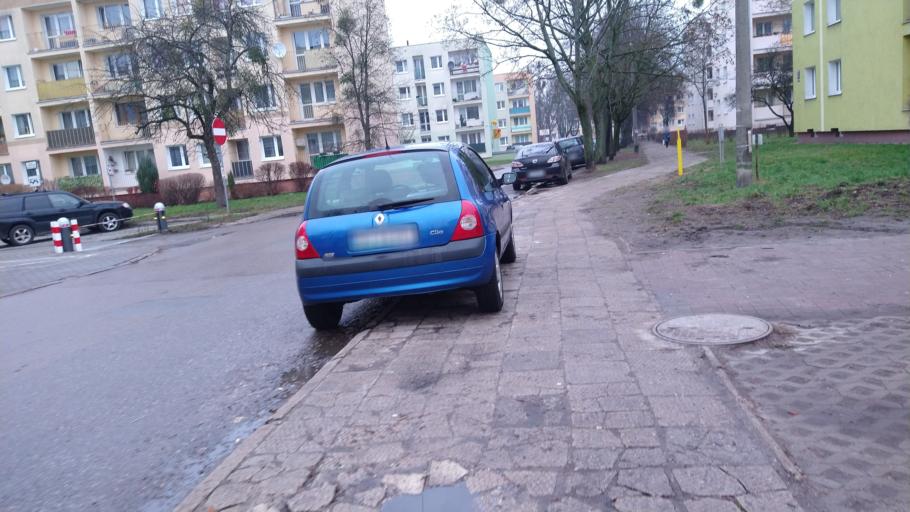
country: PL
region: Warmian-Masurian Voivodeship
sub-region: Powiat olsztynski
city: Olsztyn
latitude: 53.7892
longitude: 20.4969
